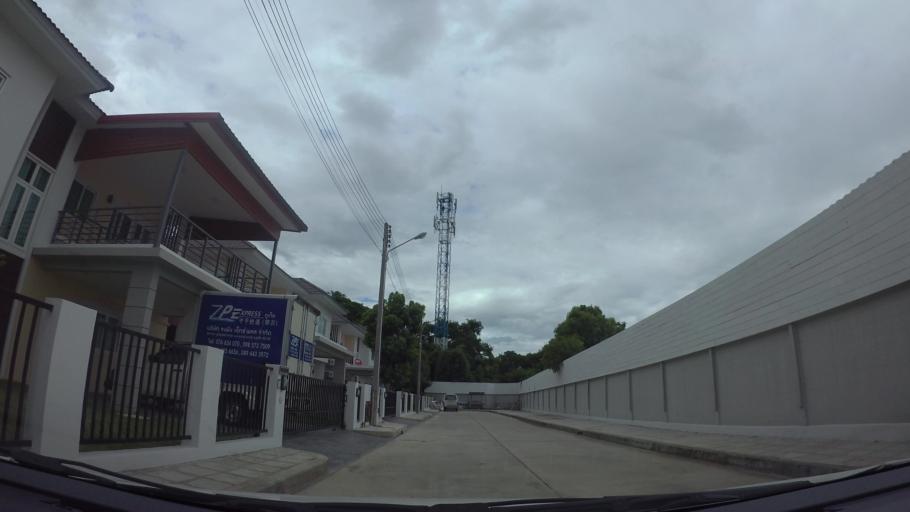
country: TH
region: Chiang Mai
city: Saraphi
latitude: 18.7511
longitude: 99.0532
